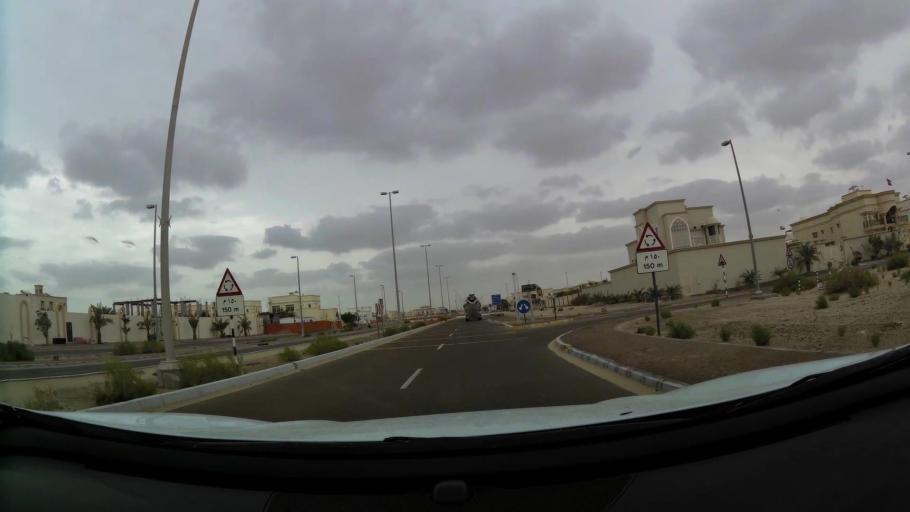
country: AE
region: Abu Dhabi
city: Abu Dhabi
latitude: 24.3749
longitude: 54.6434
